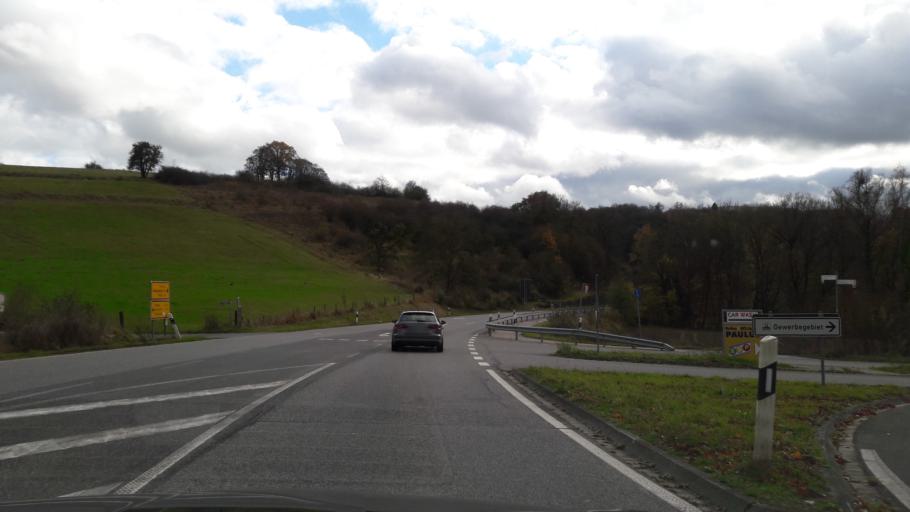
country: DE
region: Rheinland-Pfalz
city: Echternacherbruck
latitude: 49.8156
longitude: 6.4418
